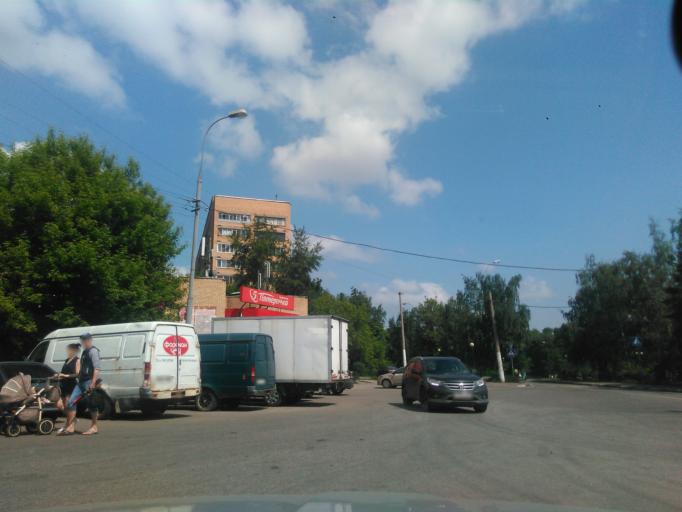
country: RU
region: Moscow
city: Vagonoremont
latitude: 55.8937
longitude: 37.5349
